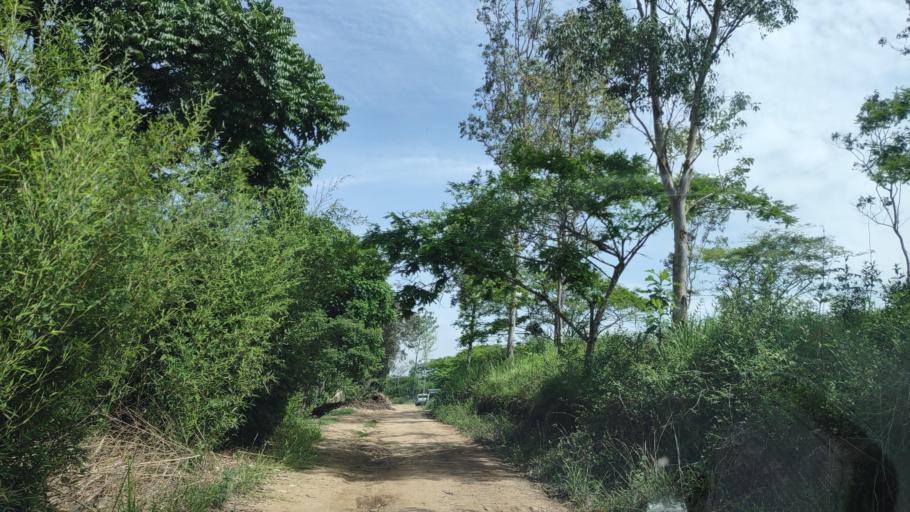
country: MX
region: Veracruz
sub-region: Emiliano Zapata
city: Dos Rios
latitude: 19.4717
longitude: -96.8299
